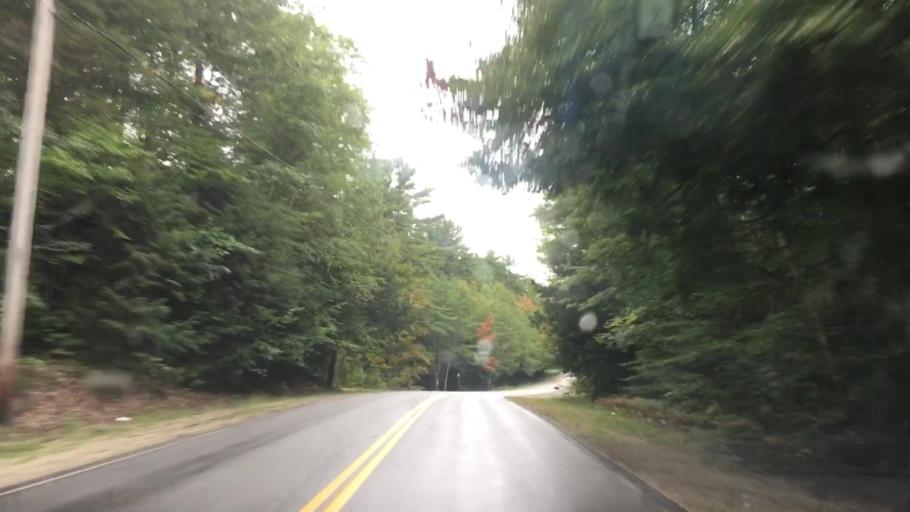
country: US
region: Maine
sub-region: Cumberland County
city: Raymond
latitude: 43.9310
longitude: -70.4078
